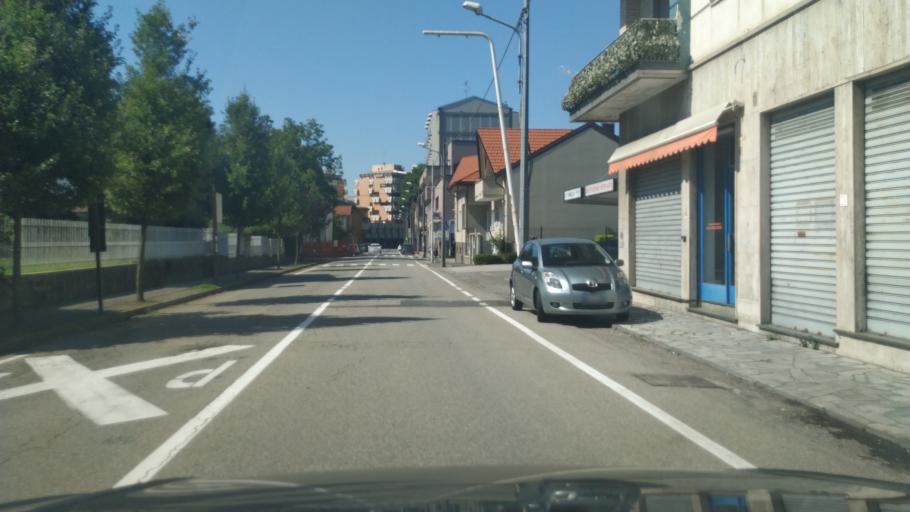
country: IT
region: Piedmont
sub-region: Provincia di Novara
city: Borgomanero
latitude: 45.7020
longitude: 8.4668
